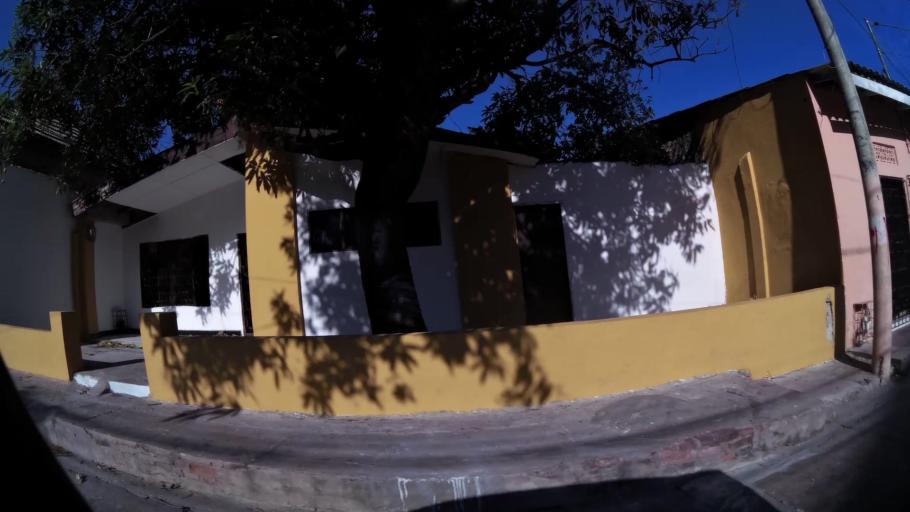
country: CO
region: Atlantico
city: Barranquilla
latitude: 10.9912
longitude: -74.7824
